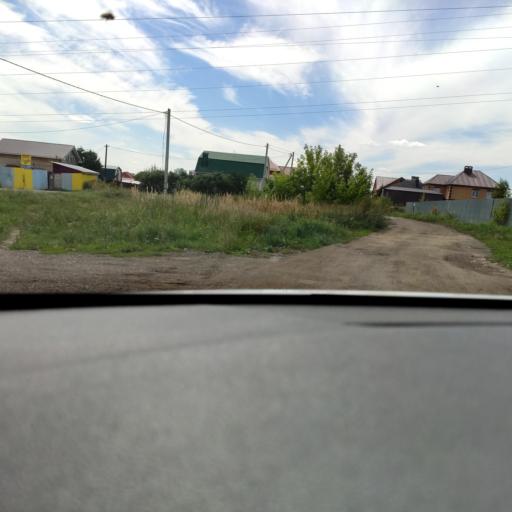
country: RU
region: Tatarstan
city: Vysokaya Gora
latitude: 55.8037
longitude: 49.2553
